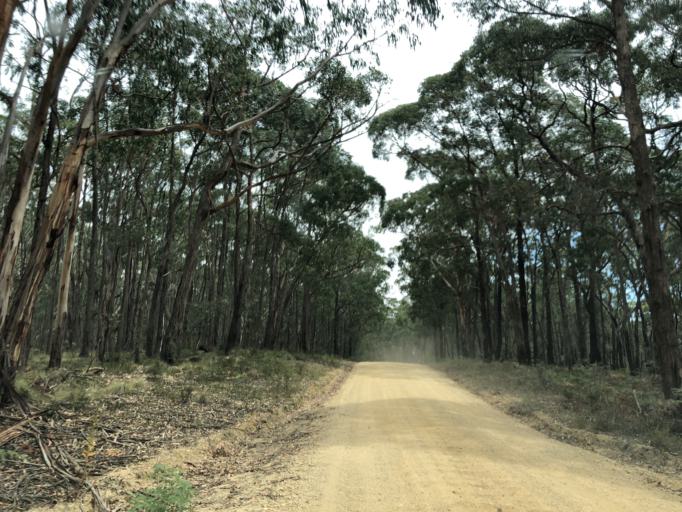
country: AU
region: Victoria
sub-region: Moorabool
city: Bacchus Marsh
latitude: -37.5002
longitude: 144.3389
